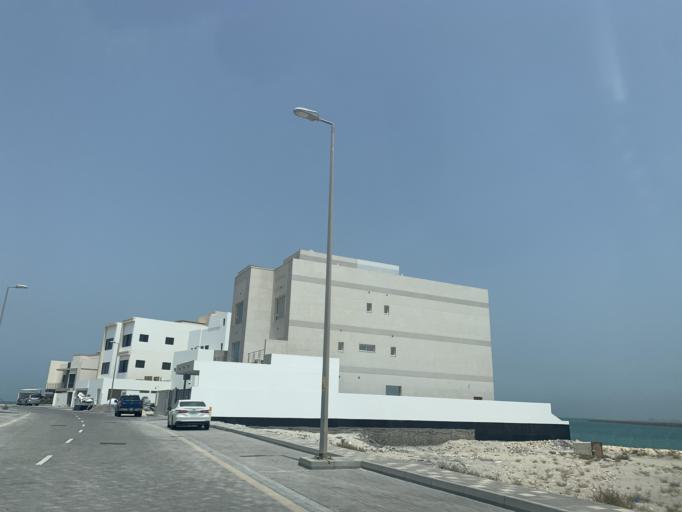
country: BH
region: Muharraq
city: Al Hadd
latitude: 26.2691
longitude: 50.6789
